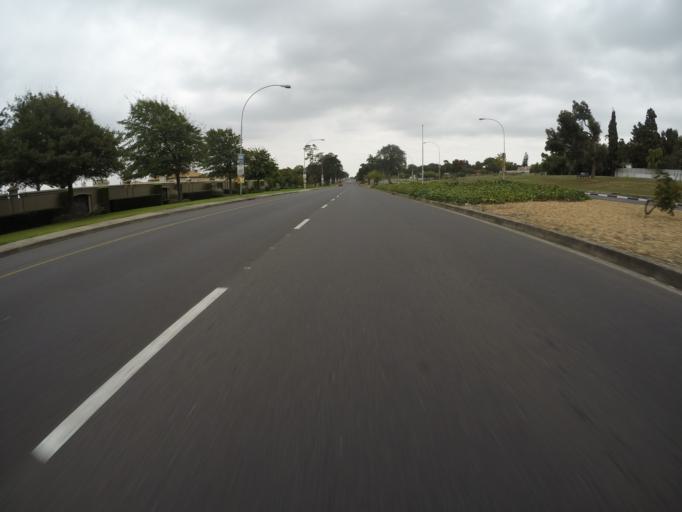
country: ZA
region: Western Cape
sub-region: City of Cape Town
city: Kraaifontein
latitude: -33.8488
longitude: 18.6443
